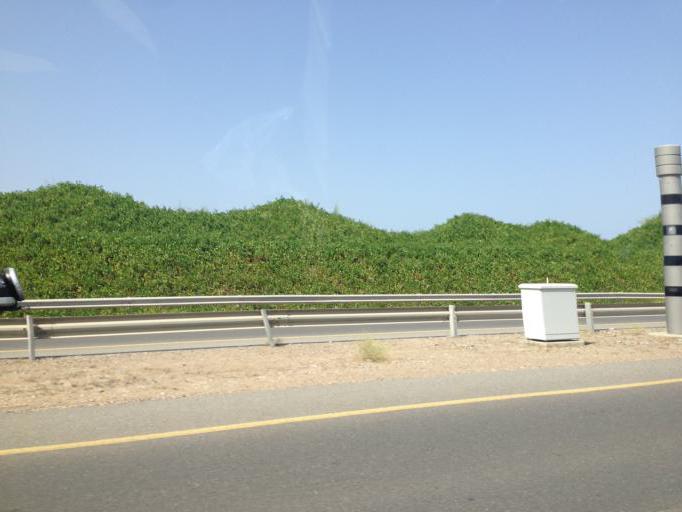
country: OM
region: Muhafazat Masqat
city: As Sib al Jadidah
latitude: 23.6141
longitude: 58.2933
